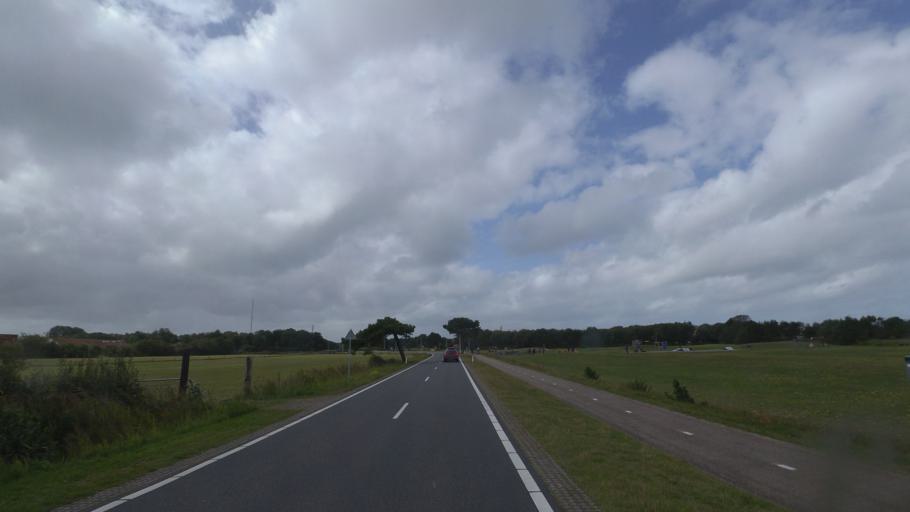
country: NL
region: Friesland
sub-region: Gemeente Ameland
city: Hollum
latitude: 53.4463
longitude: 5.6448
